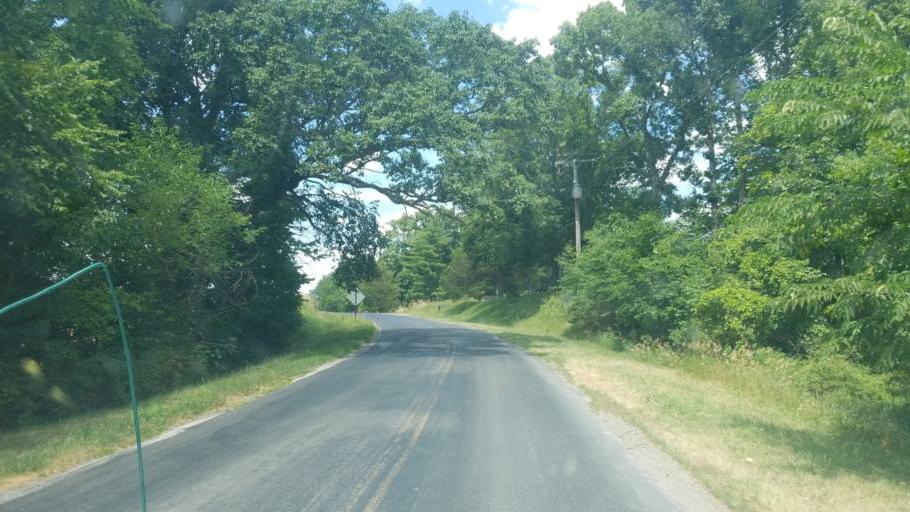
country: US
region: Ohio
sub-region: Williams County
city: Edgerton
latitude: 41.4550
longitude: -84.7106
